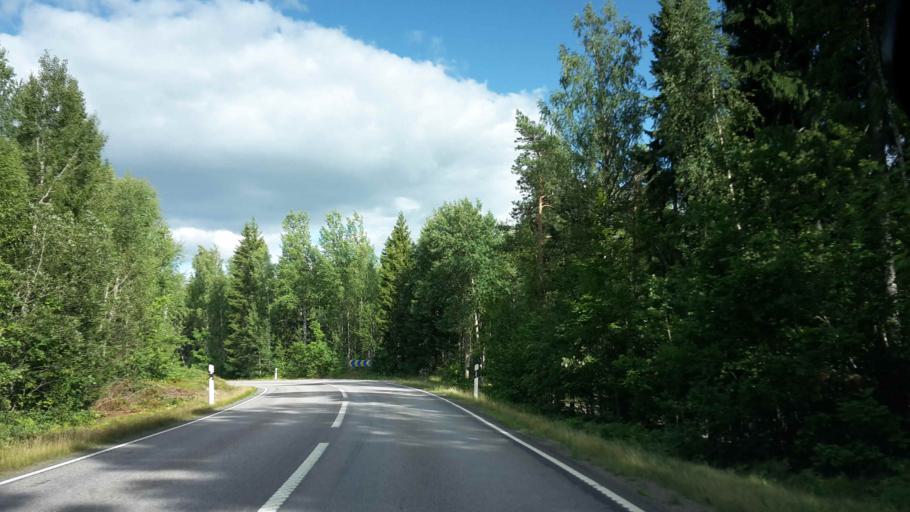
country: SE
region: OEstergoetland
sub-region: Motala Kommun
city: Borensberg
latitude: 58.8019
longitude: 15.4237
